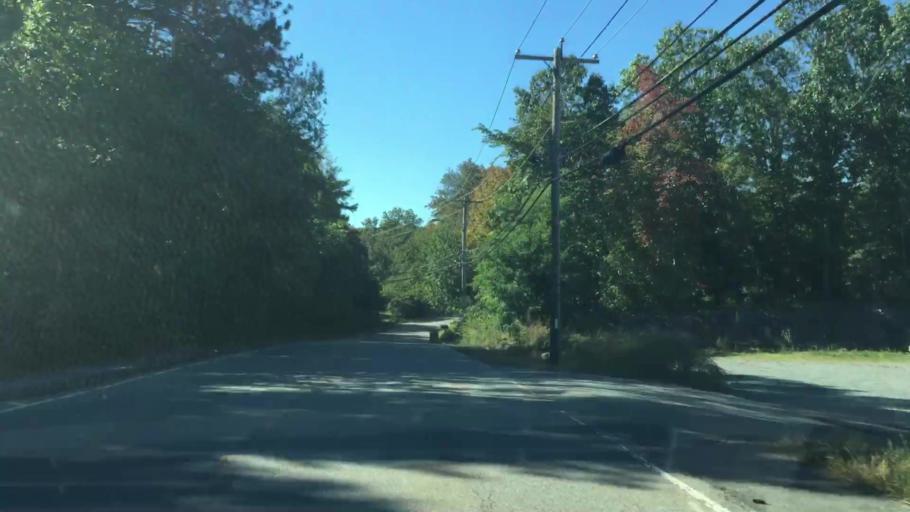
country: US
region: Massachusetts
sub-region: Essex County
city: North Andover
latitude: 42.6831
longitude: -71.0850
